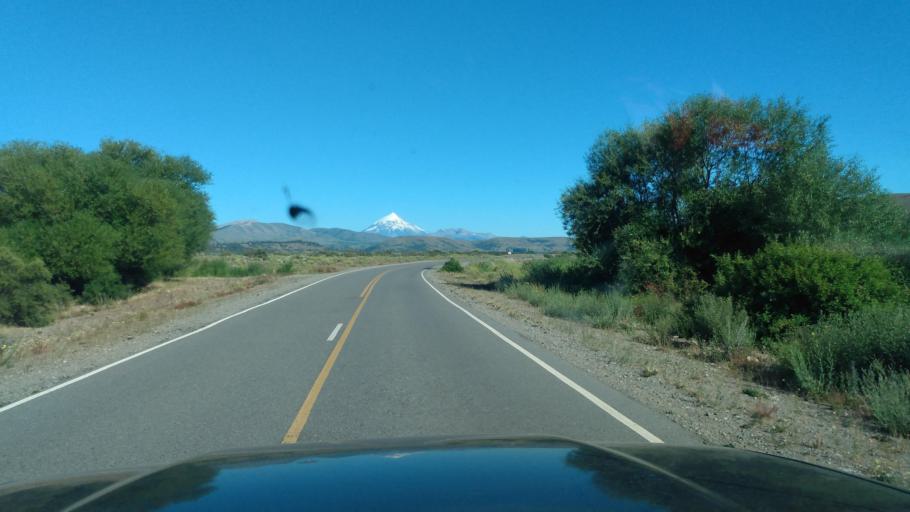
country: AR
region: Neuquen
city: Junin de los Andes
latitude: -39.8936
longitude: -71.1492
